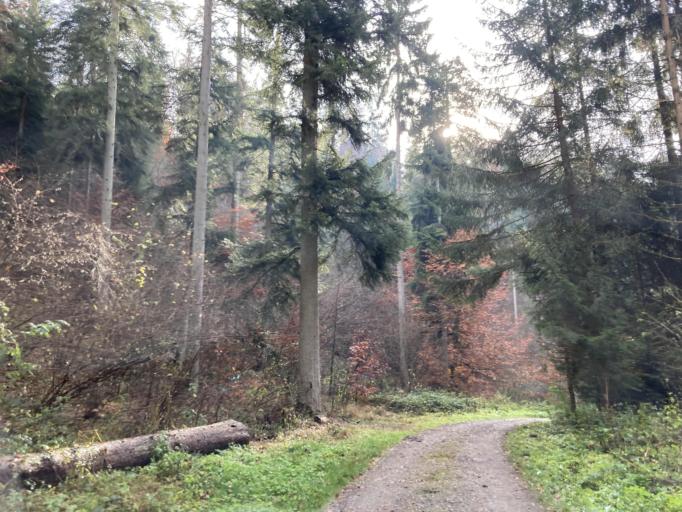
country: DE
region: Baden-Wuerttemberg
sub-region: Regierungsbezirk Stuttgart
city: Bondorf
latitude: 48.4769
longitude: 8.8347
